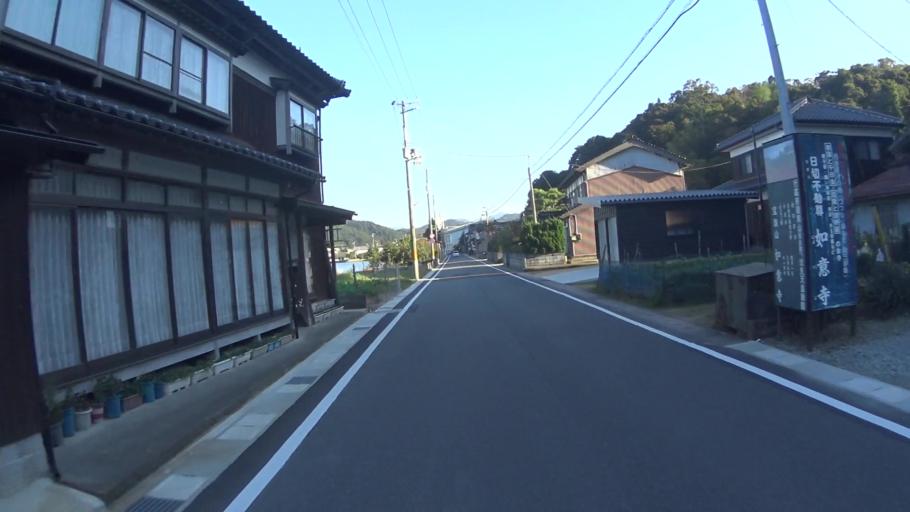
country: JP
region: Hyogo
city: Toyooka
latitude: 35.6097
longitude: 134.8903
